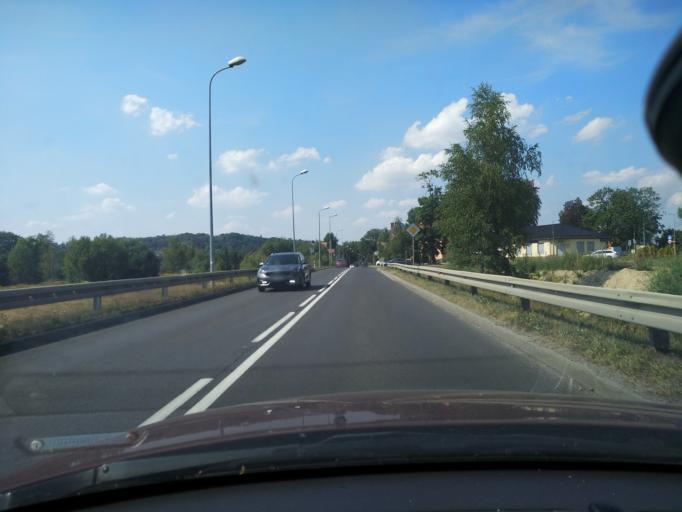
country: PL
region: Lower Silesian Voivodeship
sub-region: Powiat lubanski
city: Luban
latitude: 51.1083
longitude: 15.3032
